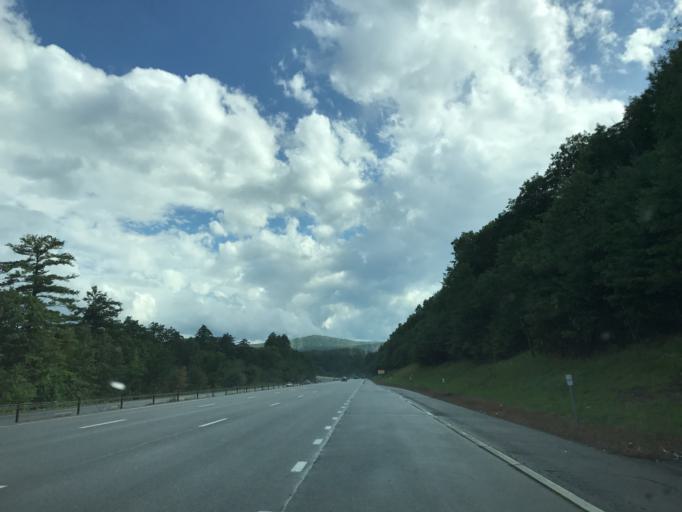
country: US
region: New York
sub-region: Warren County
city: Warrensburg
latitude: 43.4217
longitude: -73.7220
